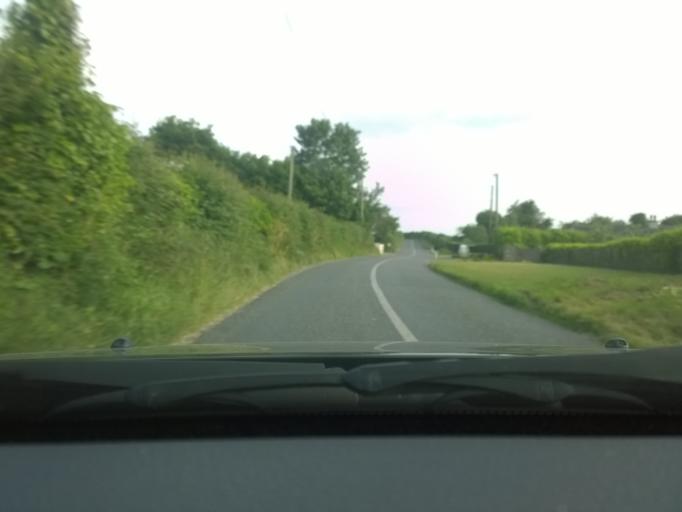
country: IE
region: Leinster
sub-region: Kildare
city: Kildare
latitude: 53.1840
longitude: -6.9299
